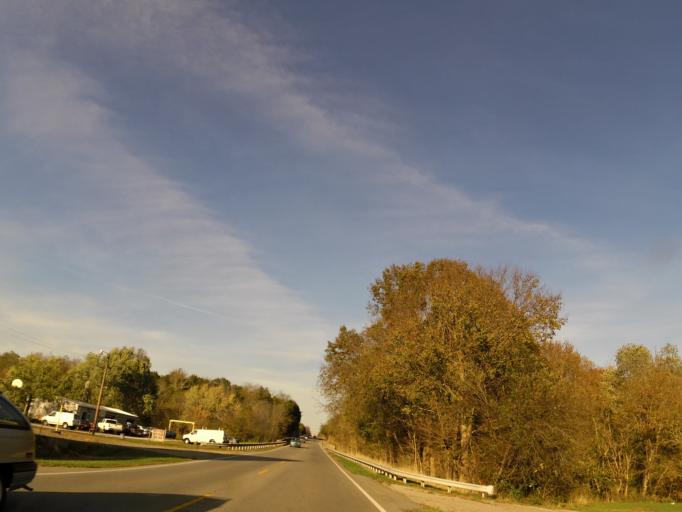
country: US
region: Kentucky
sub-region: Lincoln County
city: Stanford
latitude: 37.5695
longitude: -84.6174
